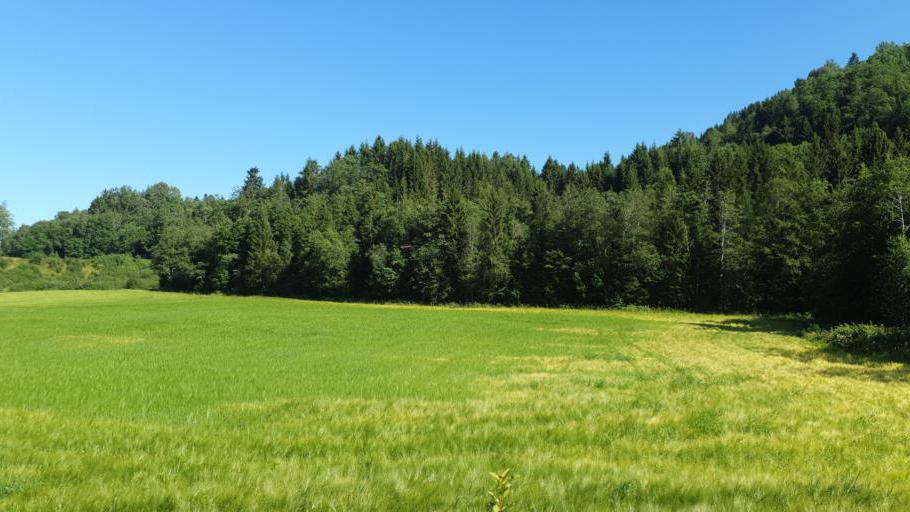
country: NO
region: Sor-Trondelag
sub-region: Orkdal
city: Orkanger
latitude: 63.1957
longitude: 9.7868
